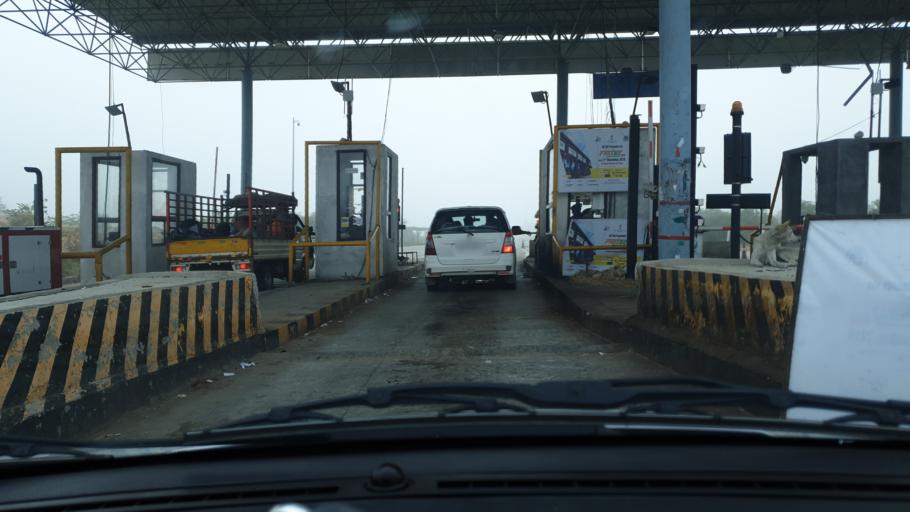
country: IN
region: Telangana
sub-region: Nalgonda
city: Devarkonda
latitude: 16.6122
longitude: 78.6759
